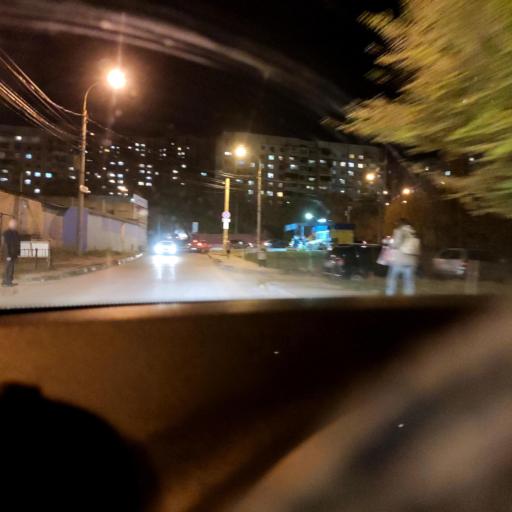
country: RU
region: Samara
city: Samara
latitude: 53.2462
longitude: 50.1918
